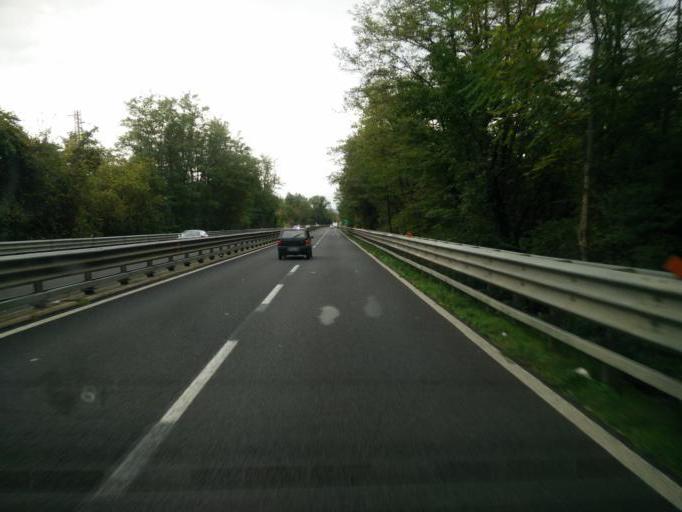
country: IT
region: Tuscany
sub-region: Province of Florence
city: Sambuca
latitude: 43.6014
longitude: 11.1929
